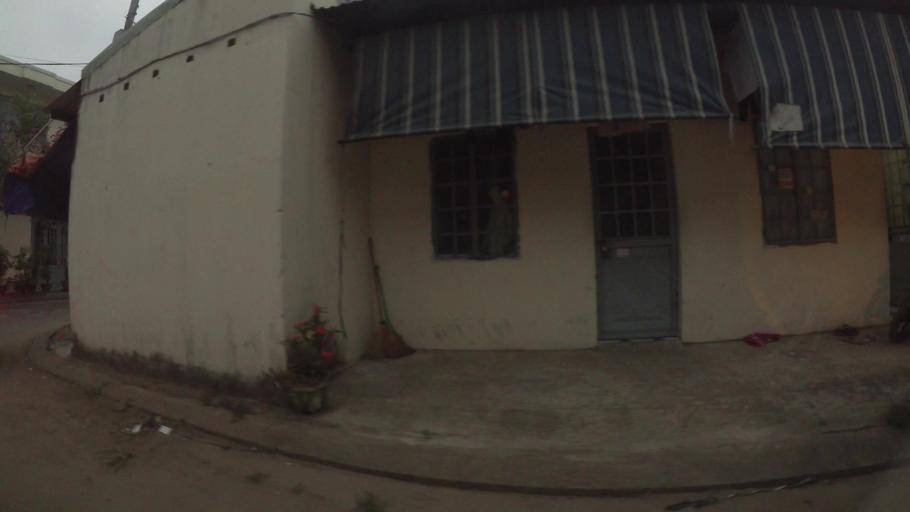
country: VN
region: Da Nang
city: Lien Chieu
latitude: 16.0550
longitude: 108.1705
